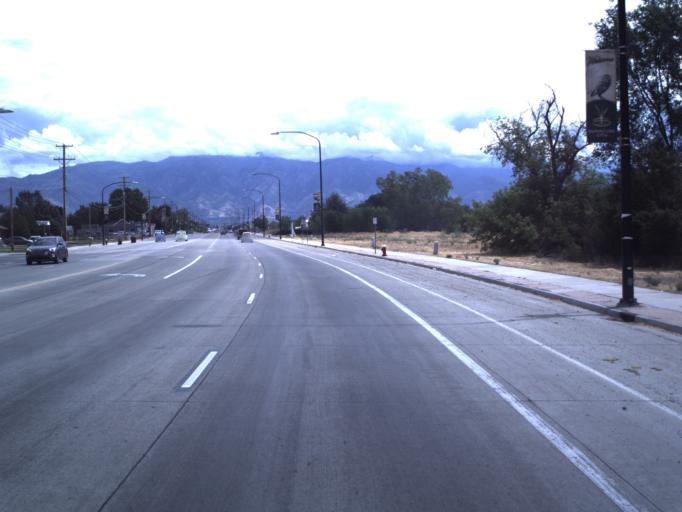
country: US
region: Utah
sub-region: Davis County
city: Syracuse
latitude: 41.0890
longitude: -112.0605
